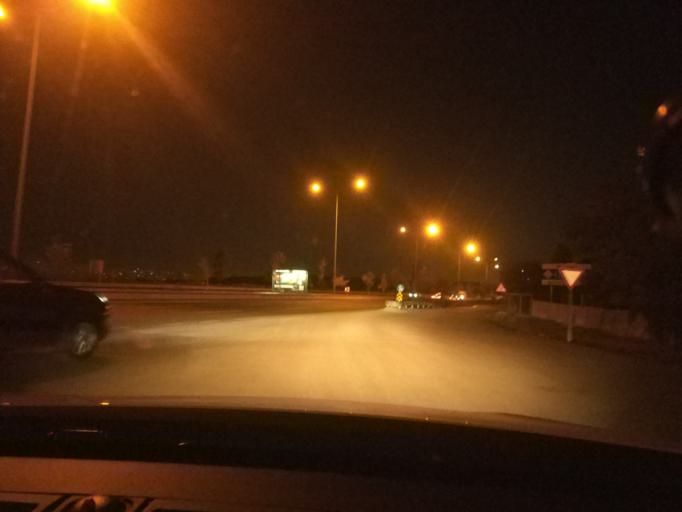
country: TR
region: Ankara
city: Batikent
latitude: 39.9147
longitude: 32.7534
